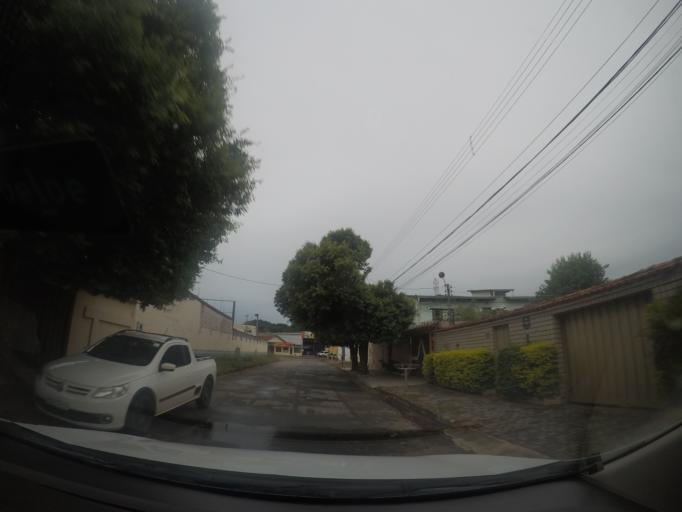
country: BR
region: Goias
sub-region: Goiania
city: Goiania
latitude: -16.6394
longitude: -49.2416
